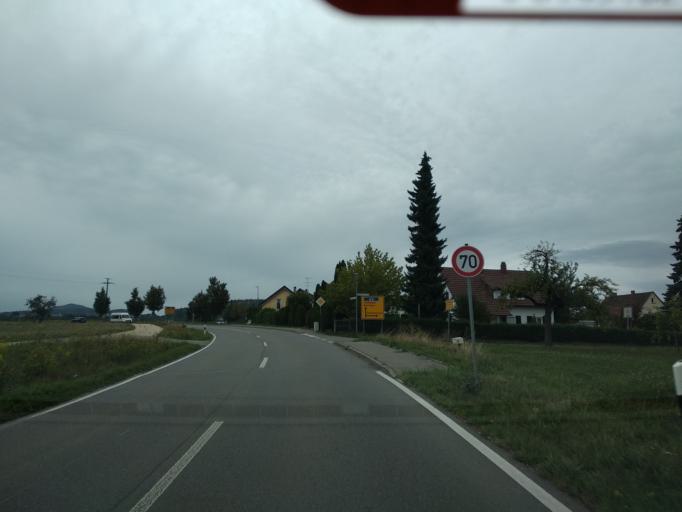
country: DE
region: Baden-Wuerttemberg
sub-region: Freiburg Region
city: Gottmadingen
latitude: 47.7278
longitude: 8.7560
